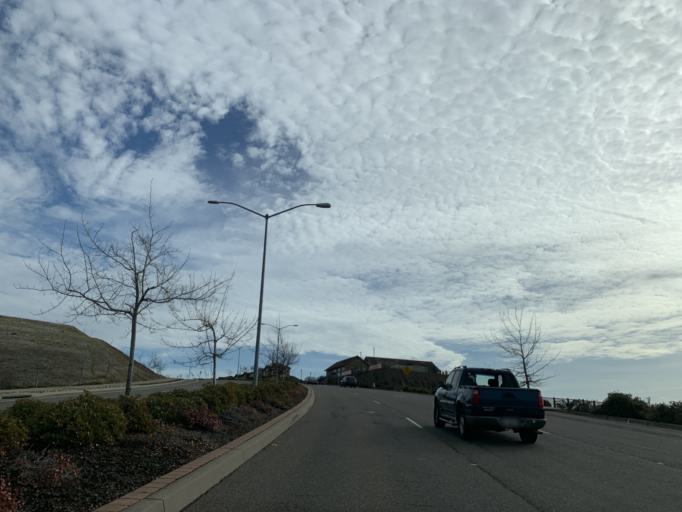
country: US
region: California
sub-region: El Dorado County
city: El Dorado Hills
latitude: 38.6470
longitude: -121.1013
